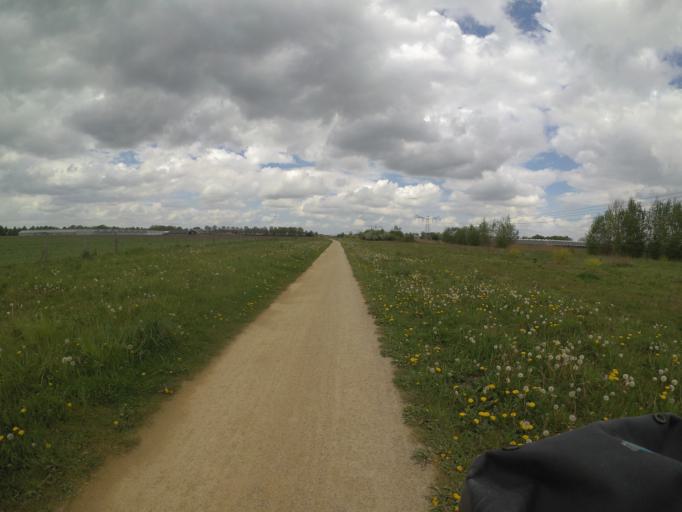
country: NL
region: North Brabant
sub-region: Gemeente Dongen
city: Dongen
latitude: 51.6317
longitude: 4.9602
